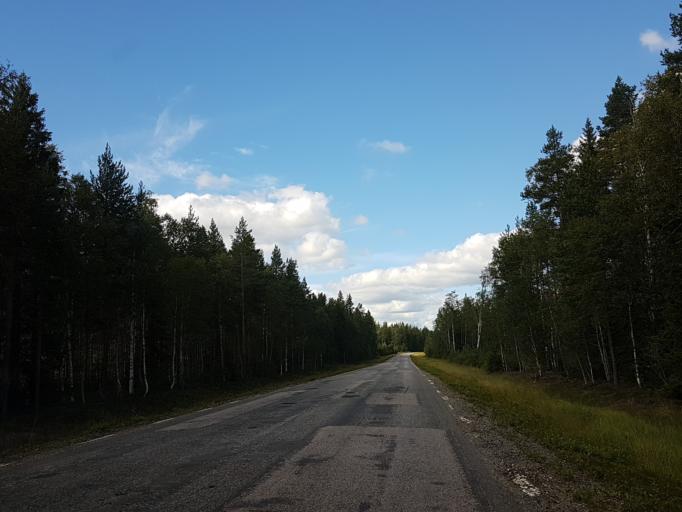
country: SE
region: Vaesterbotten
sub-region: Skelleftea Kommun
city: Burtraesk
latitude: 64.2470
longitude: 20.4804
